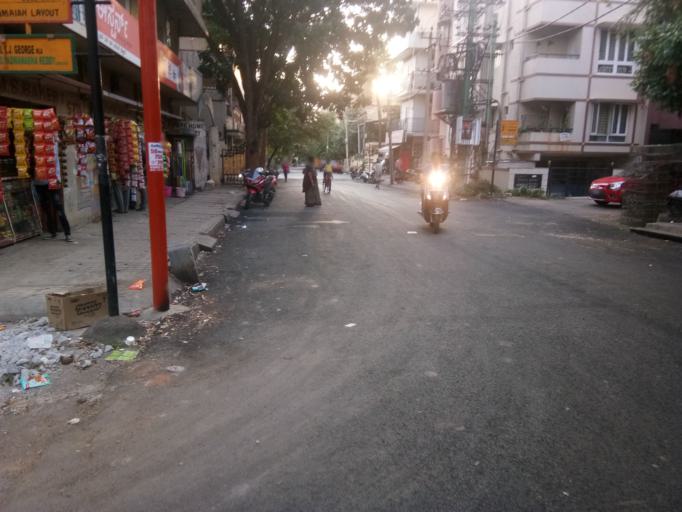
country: IN
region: Karnataka
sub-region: Bangalore Urban
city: Bangalore
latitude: 13.0186
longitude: 77.6337
